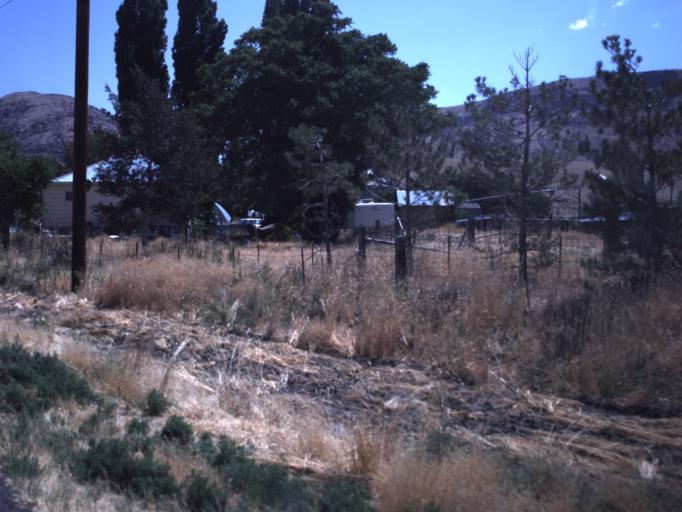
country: US
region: Utah
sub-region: Millard County
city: Delta
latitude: 39.4705
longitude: -112.2713
